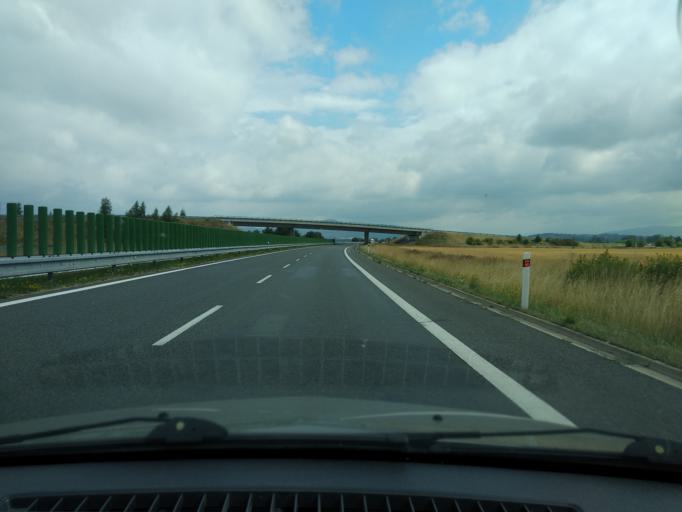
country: CZ
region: Olomoucky
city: Postrelmov
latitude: 49.9048
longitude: 16.8949
